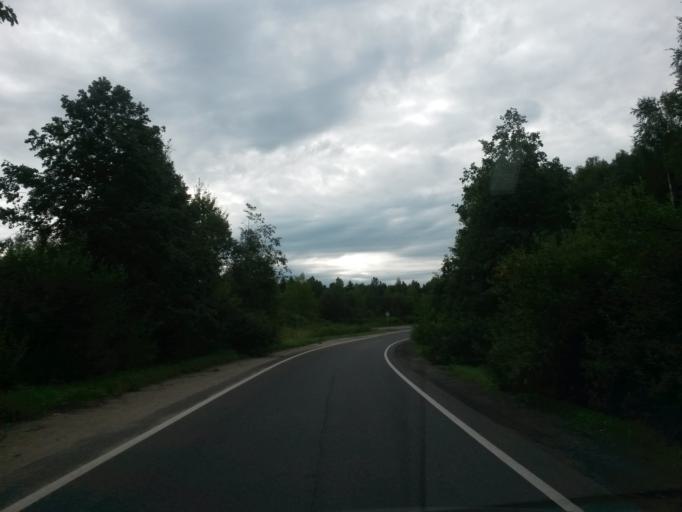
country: RU
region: Jaroslavl
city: Krasnyye Tkachi
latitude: 57.4036
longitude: 39.6584
